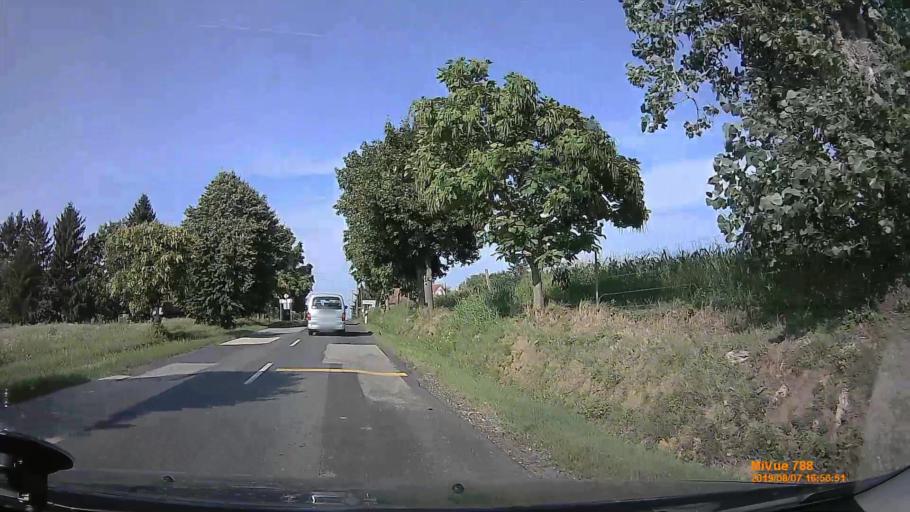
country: HU
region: Zala
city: Zalaegerszeg
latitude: 46.6949
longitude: 16.7504
